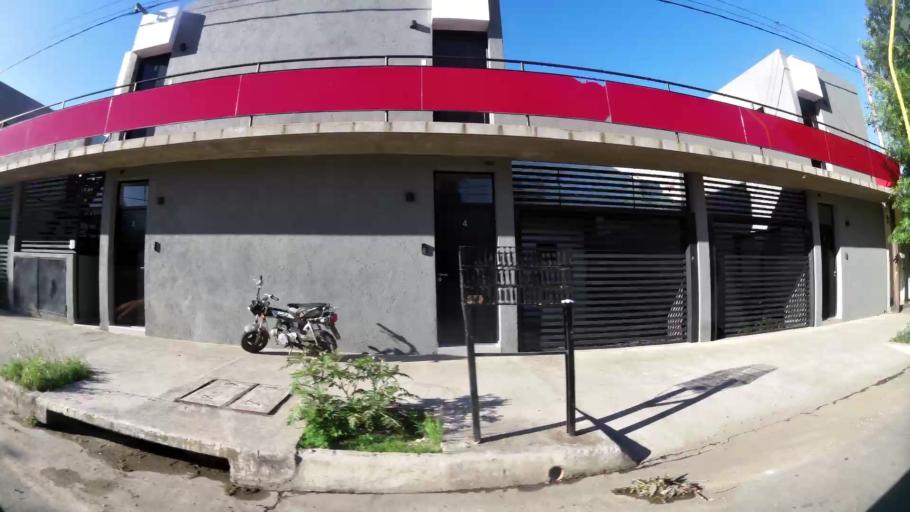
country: AR
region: Cordoba
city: San Francisco
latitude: -31.4433
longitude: -62.0999
